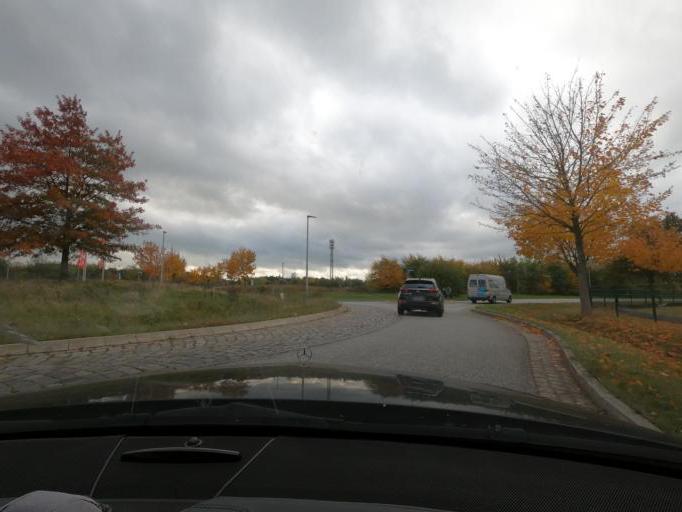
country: DE
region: Schleswig-Holstein
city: Geesthacht
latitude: 53.4555
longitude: 10.3679
